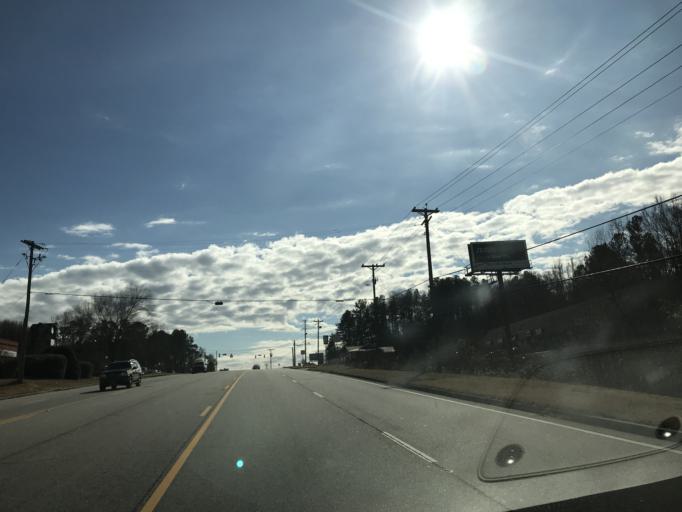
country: US
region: Georgia
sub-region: Paulding County
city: Hiram
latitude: 33.8673
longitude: -84.7641
